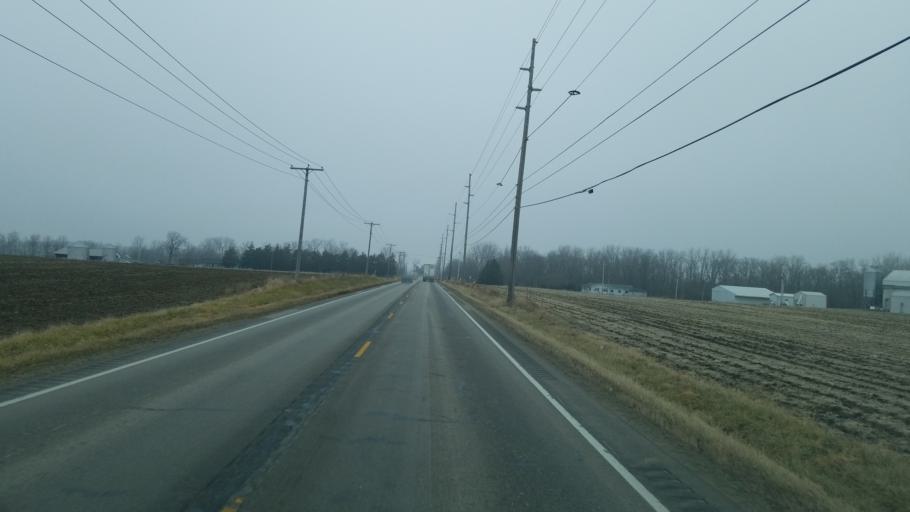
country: US
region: Indiana
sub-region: Adams County
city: Geneva
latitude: 40.5614
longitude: -84.9601
